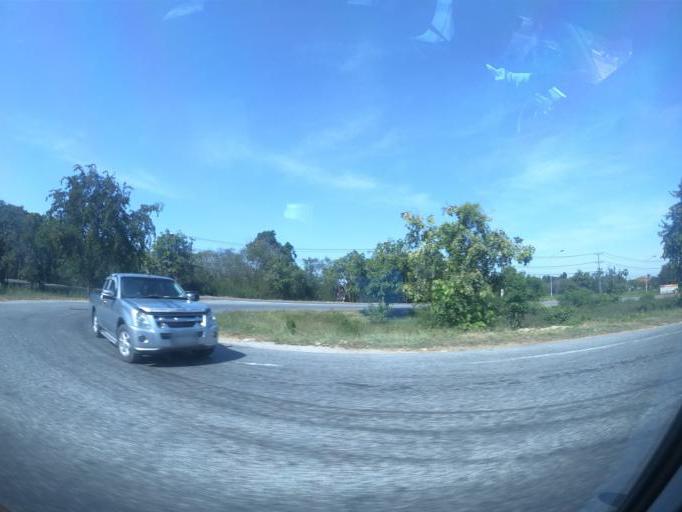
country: TH
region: Khon Kaen
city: Khon Kaen
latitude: 16.3903
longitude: 102.8095
